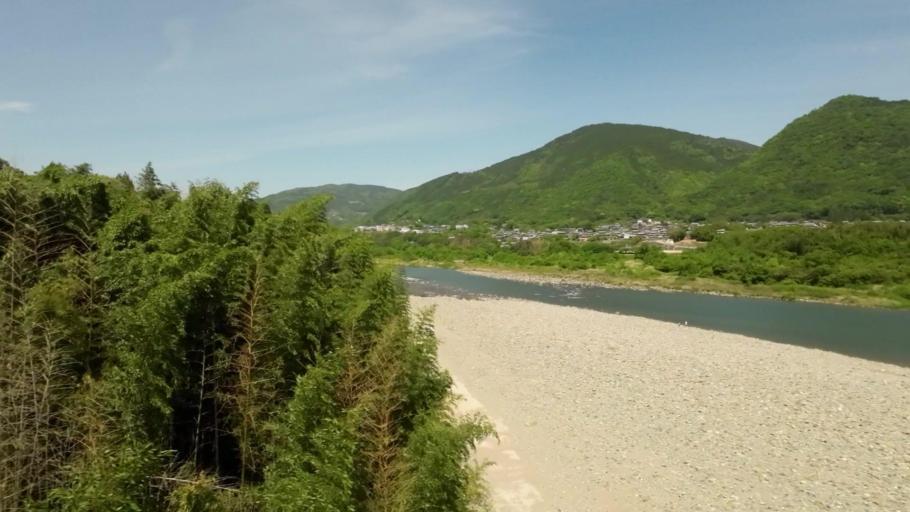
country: JP
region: Tokushima
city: Ikedacho
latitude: 34.0350
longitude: 133.8633
